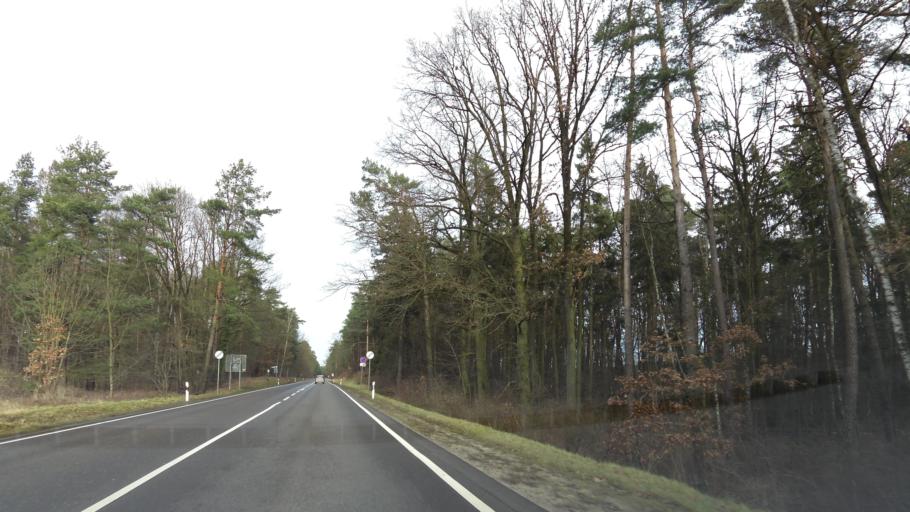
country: DE
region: Brandenburg
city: Strausberg
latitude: 52.5654
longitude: 13.8616
